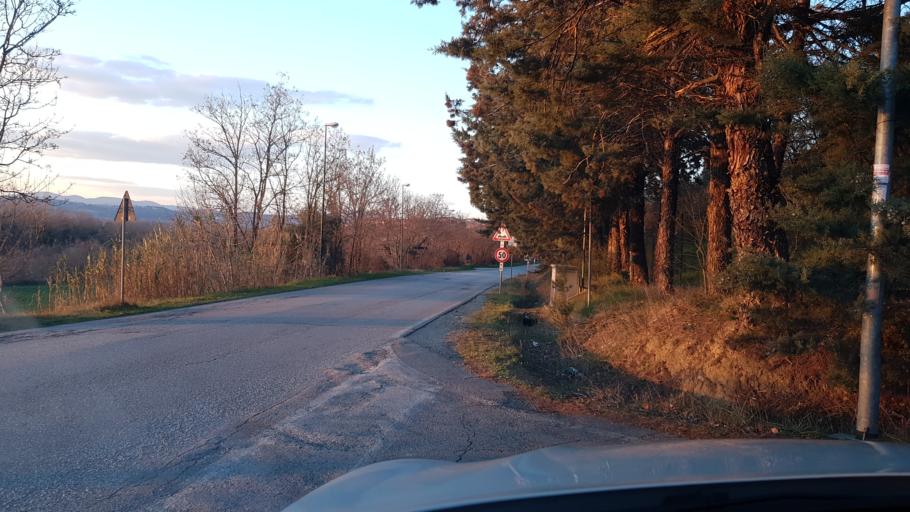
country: IT
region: Umbria
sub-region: Provincia di Perugia
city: Torgiano
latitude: 43.0149
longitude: 12.4362
